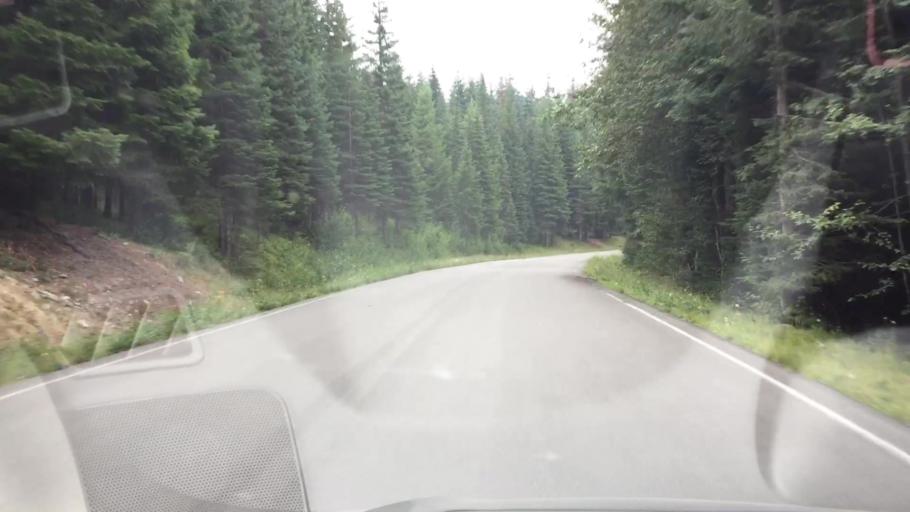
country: US
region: Washington
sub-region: Klickitat County
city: White Salmon
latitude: 46.1787
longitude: -121.6336
